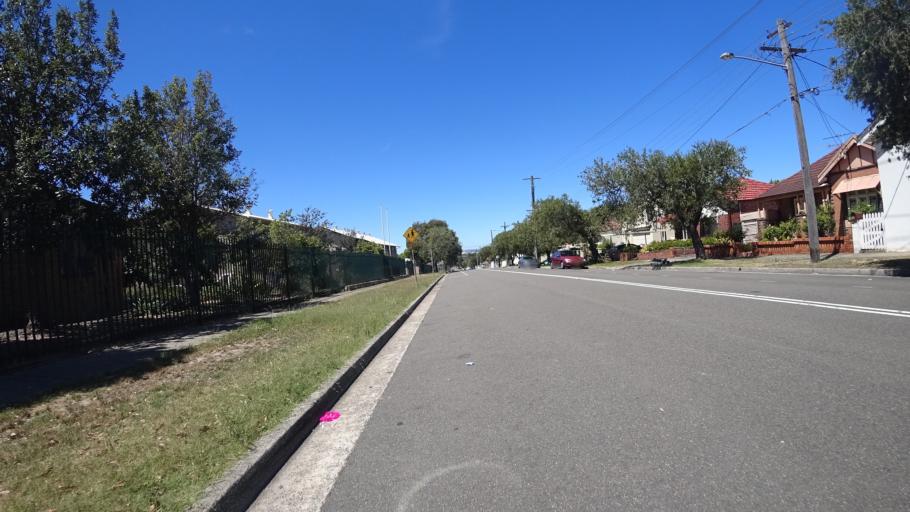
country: AU
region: New South Wales
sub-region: Rockdale
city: Bexley
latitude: -33.9638
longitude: 151.1226
